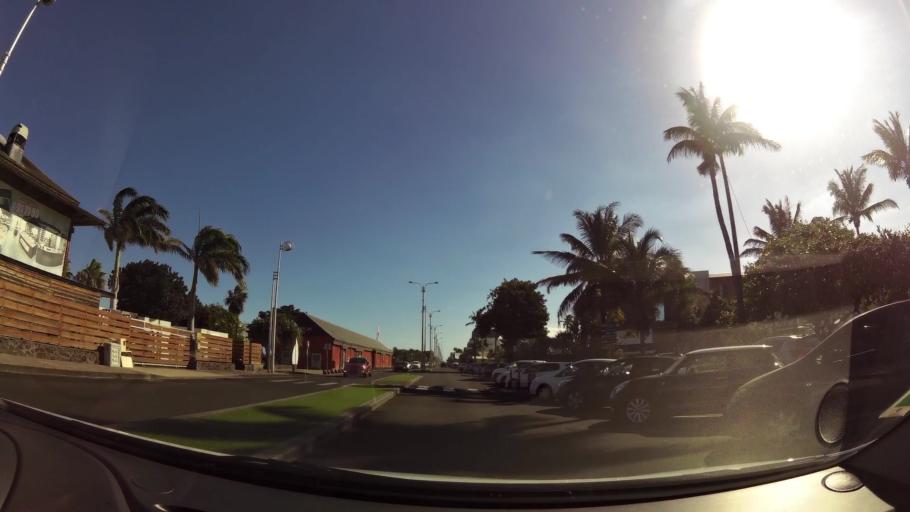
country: RE
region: Reunion
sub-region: Reunion
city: Saint-Pierre
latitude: -21.3436
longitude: 55.4778
